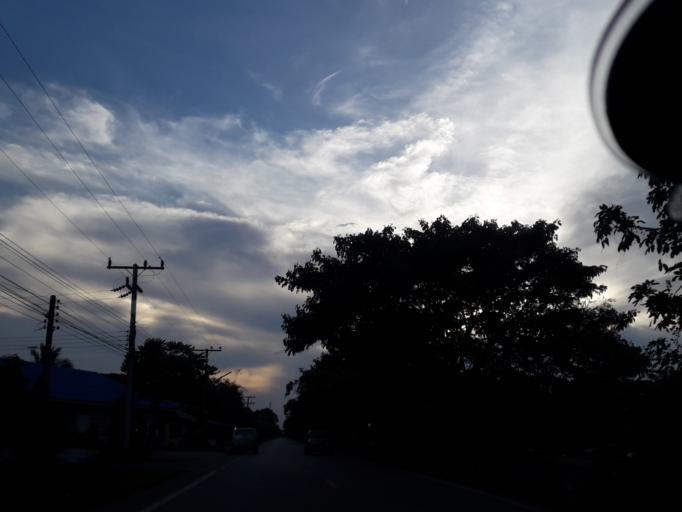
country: TH
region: Sara Buri
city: Nong Khae
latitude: 14.2671
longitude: 100.8732
